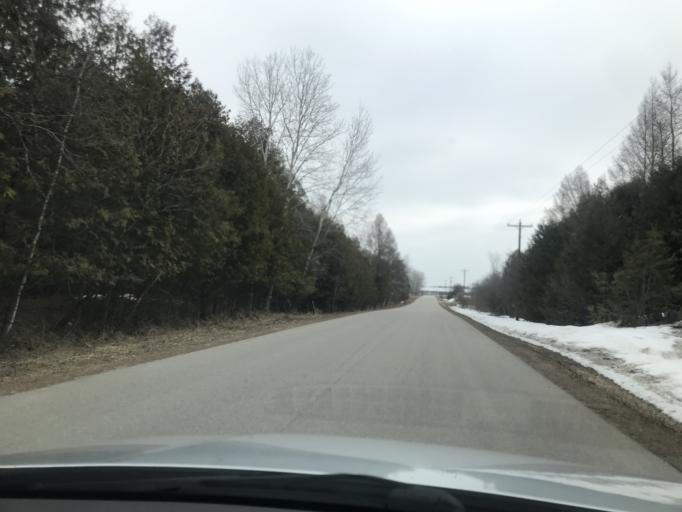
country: US
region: Wisconsin
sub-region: Marinette County
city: Peshtigo
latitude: 45.0275
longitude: -87.8663
